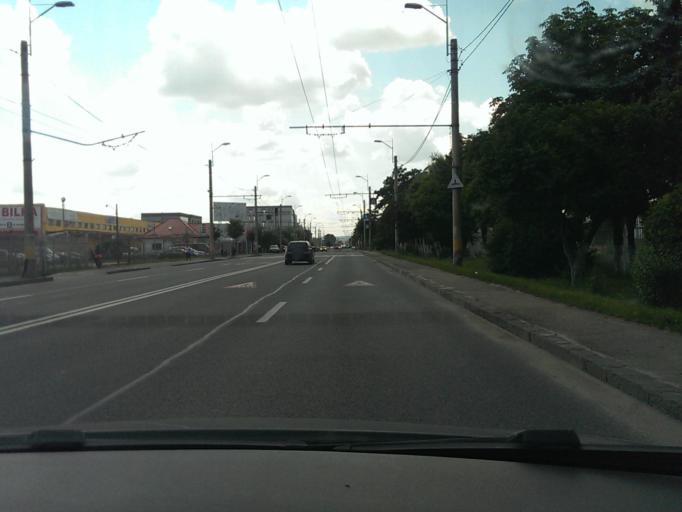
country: RO
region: Cluj
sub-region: Comuna Apahida
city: Sannicoara
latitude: 46.7818
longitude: 23.6934
